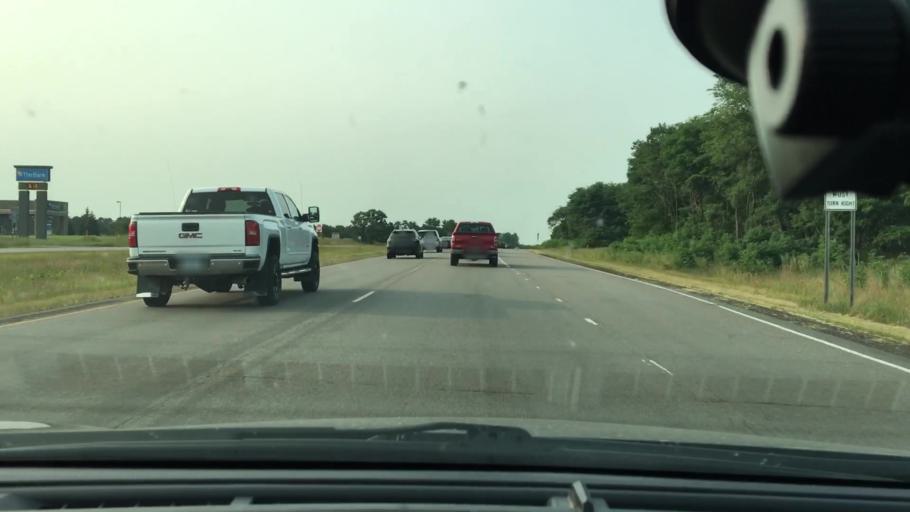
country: US
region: Minnesota
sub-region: Sherburne County
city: Zimmerman
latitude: 45.4465
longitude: -93.5848
